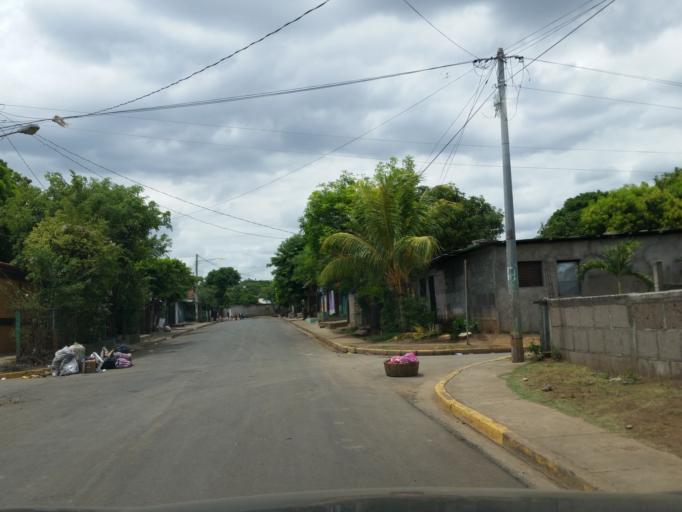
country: NI
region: Managua
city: Managua
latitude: 12.1347
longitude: -86.2629
